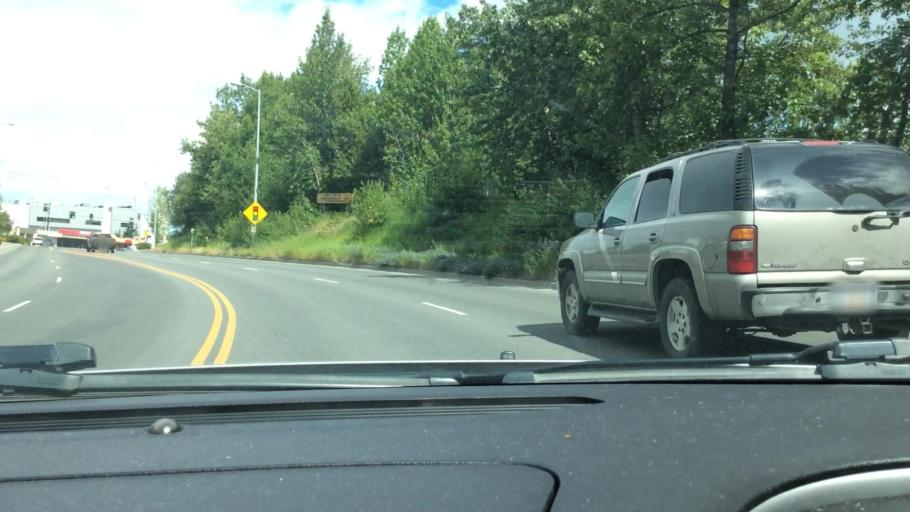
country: US
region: Alaska
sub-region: Anchorage Municipality
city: Anchorage
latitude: 61.2288
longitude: -149.8753
